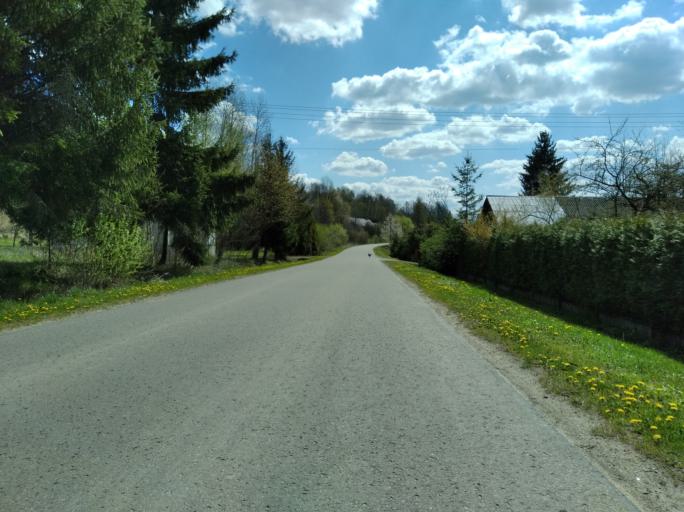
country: PL
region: Subcarpathian Voivodeship
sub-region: Powiat brzozowski
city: Wesola
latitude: 49.7817
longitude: 22.1327
